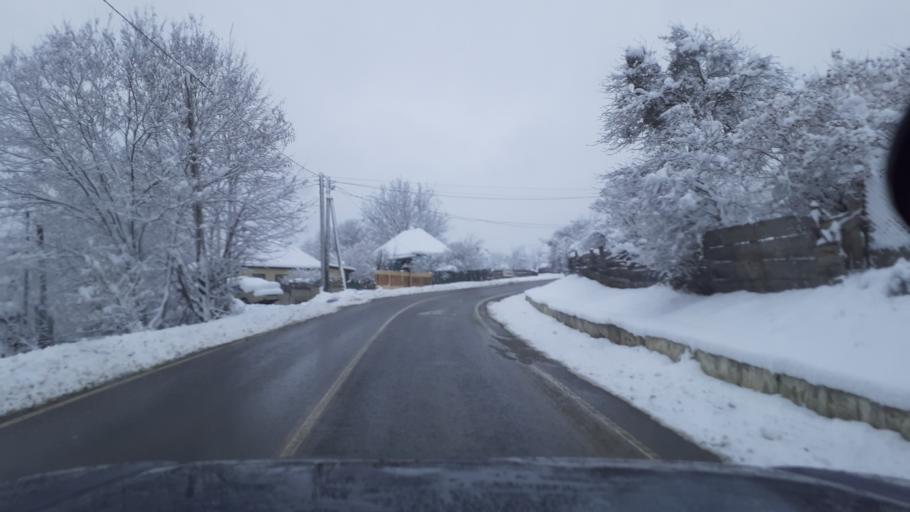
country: RU
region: Adygeya
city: Kamennomostskiy
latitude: 44.2288
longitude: 40.2027
